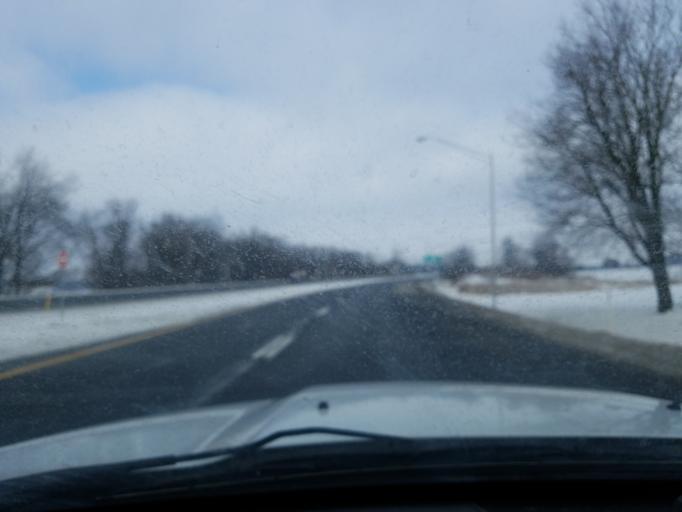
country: US
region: Indiana
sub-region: Marshall County
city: Plymouth
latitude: 41.3432
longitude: -86.2762
